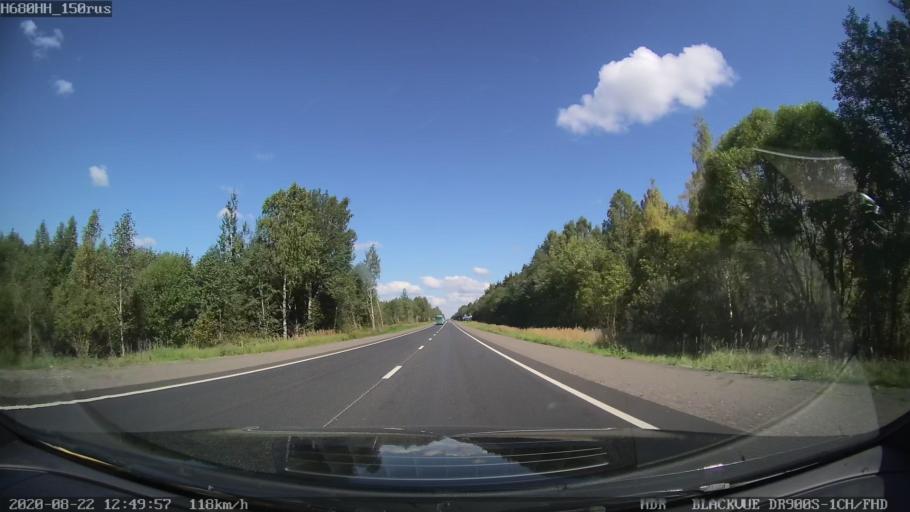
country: RU
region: Tverskaya
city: Rameshki
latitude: 57.4591
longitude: 36.2145
